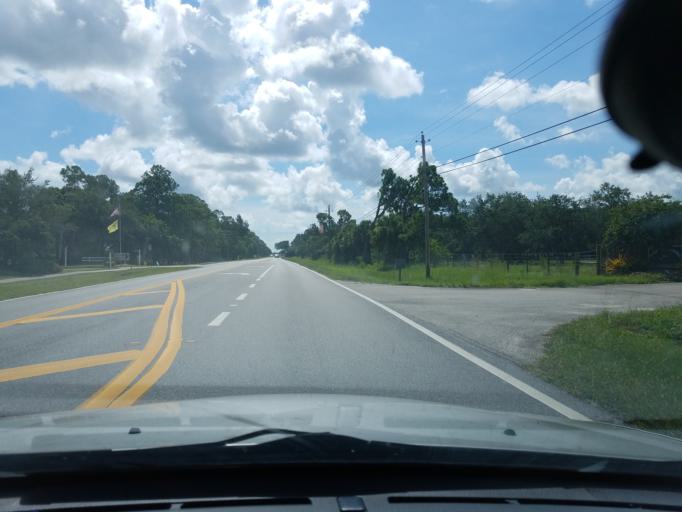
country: US
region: Florida
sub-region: Martin County
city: Palm City
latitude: 27.0881
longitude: -80.2899
